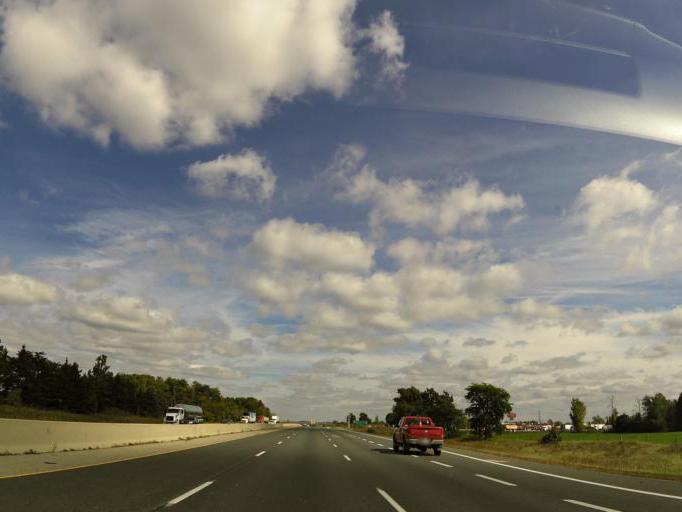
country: CA
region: Ontario
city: Dorchester
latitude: 42.9572
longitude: -81.0681
